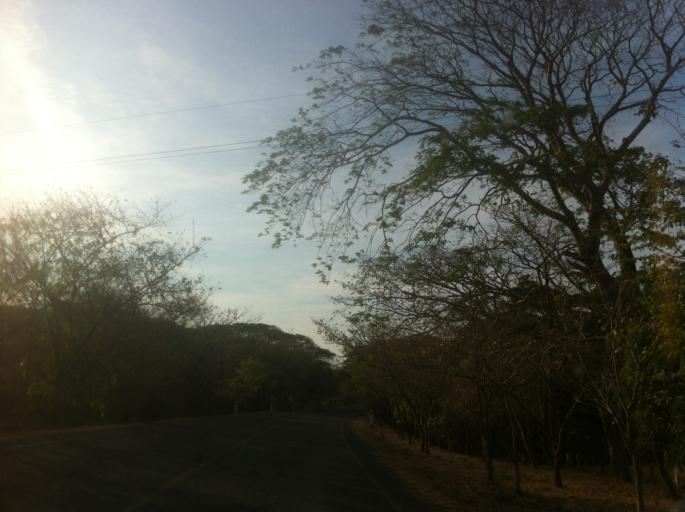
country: NI
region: Rivas
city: Cardenas
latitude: 11.2825
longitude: -85.6730
